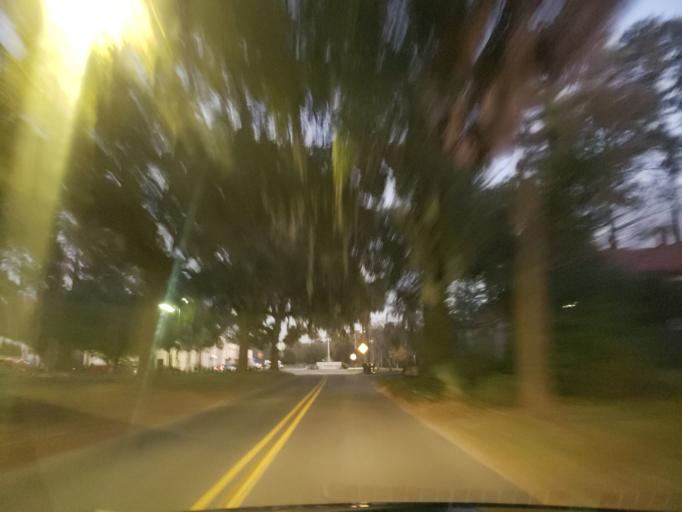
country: US
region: Georgia
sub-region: Chatham County
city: Thunderbolt
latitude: 32.0428
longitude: -81.0789
